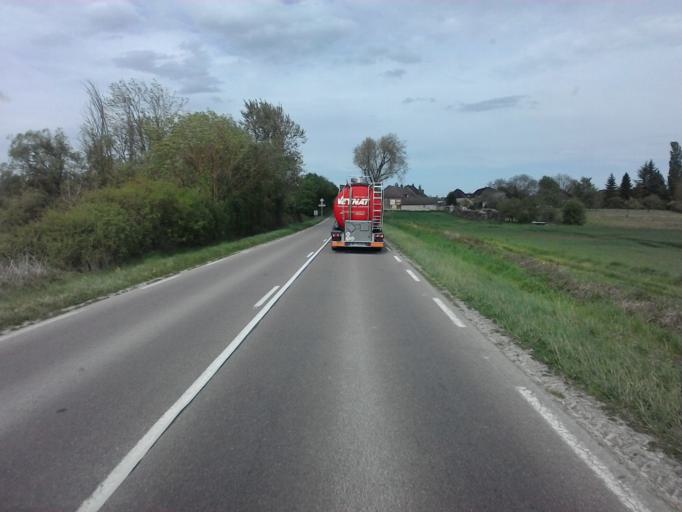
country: FR
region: Bourgogne
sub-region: Departement de l'Yonne
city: Neuvy-Sautour
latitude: 48.0351
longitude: 3.7767
